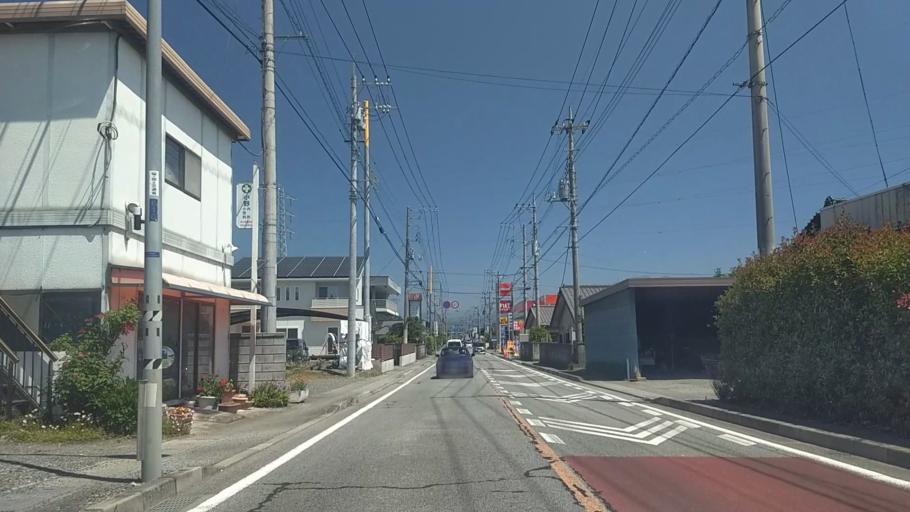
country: JP
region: Yamanashi
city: Ryuo
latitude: 35.6592
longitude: 138.4650
